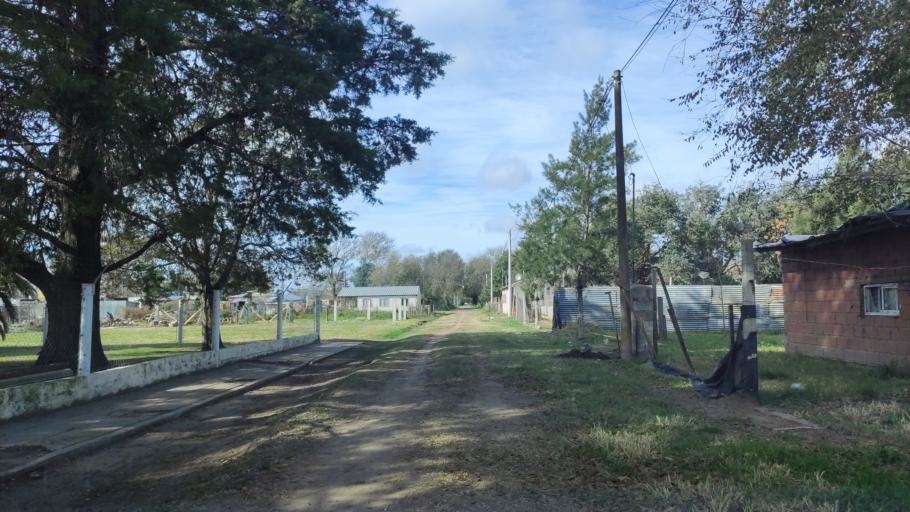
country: AR
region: Cordoba
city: General Roca
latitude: -32.7336
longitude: -61.9236
